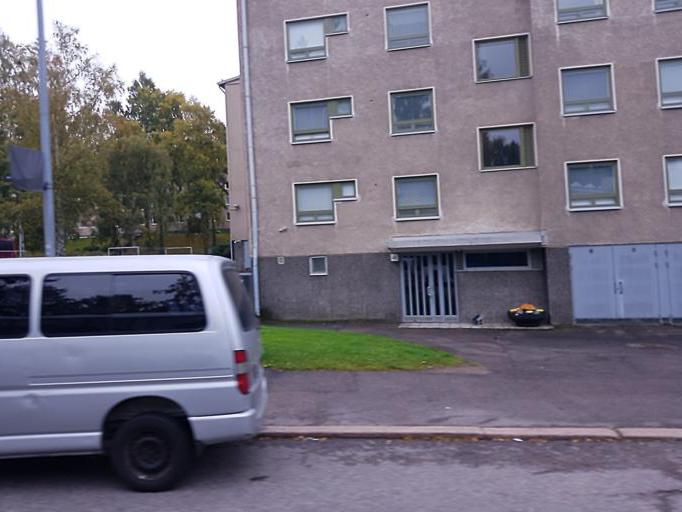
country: FI
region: Uusimaa
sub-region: Helsinki
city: Teekkarikylae
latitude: 60.2410
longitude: 24.8823
